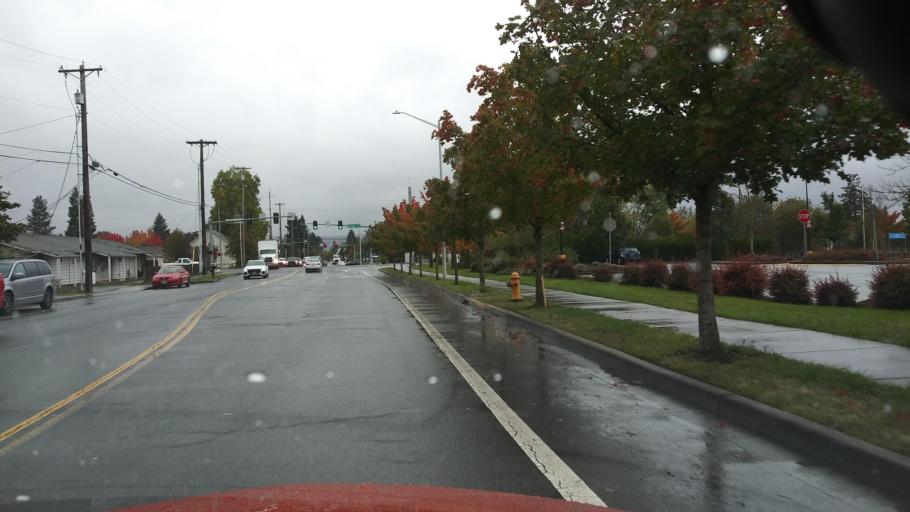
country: US
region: Oregon
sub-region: Washington County
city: Cornelius
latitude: 45.5218
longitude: -123.0668
